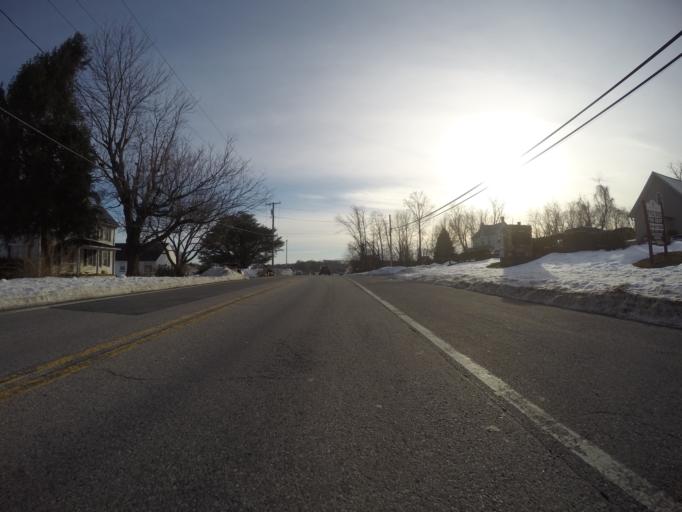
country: US
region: Maryland
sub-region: Baltimore County
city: Hunt Valley
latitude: 39.5221
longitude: -76.5589
